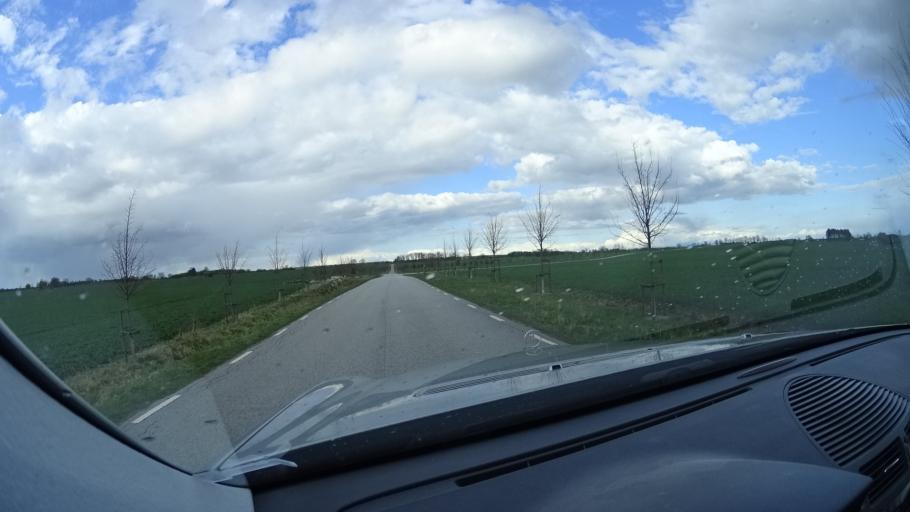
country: SE
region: Skane
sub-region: Eslovs Kommun
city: Eslov
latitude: 55.8090
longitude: 13.3761
